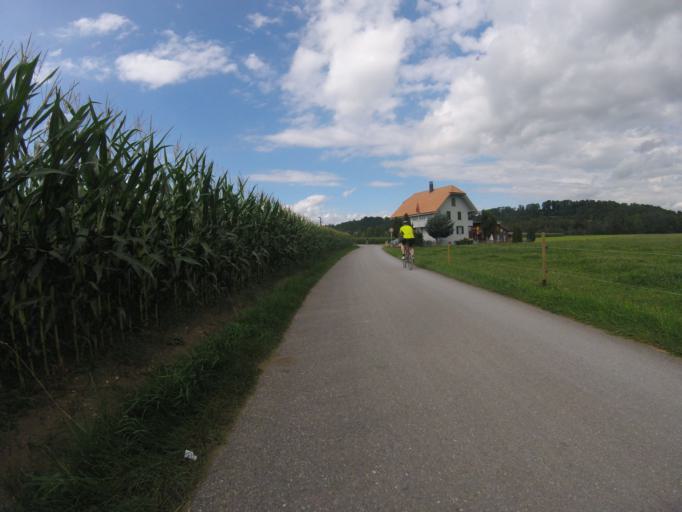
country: CH
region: Bern
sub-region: Bern-Mittelland District
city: Belp
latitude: 46.9016
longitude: 7.5133
